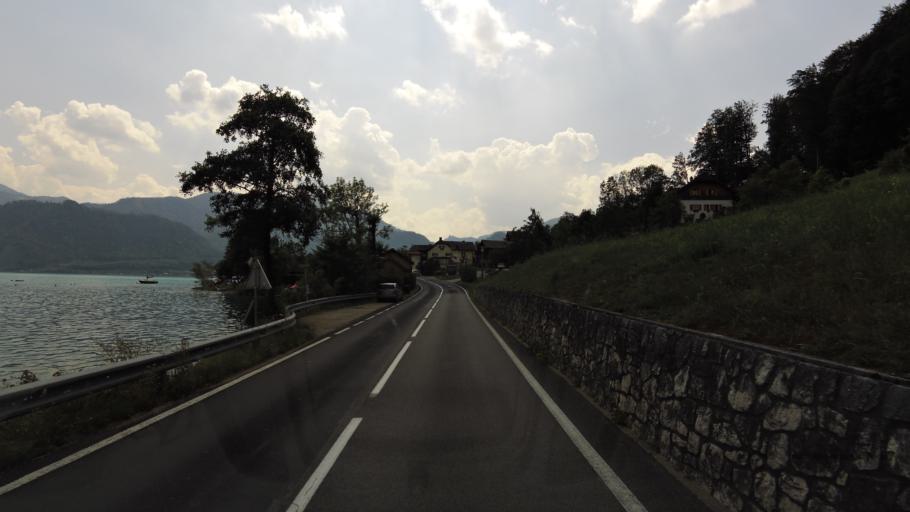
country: AT
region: Upper Austria
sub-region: Politischer Bezirk Vocklabruck
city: Steinbach am Attersee
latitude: 47.8210
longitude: 13.5090
